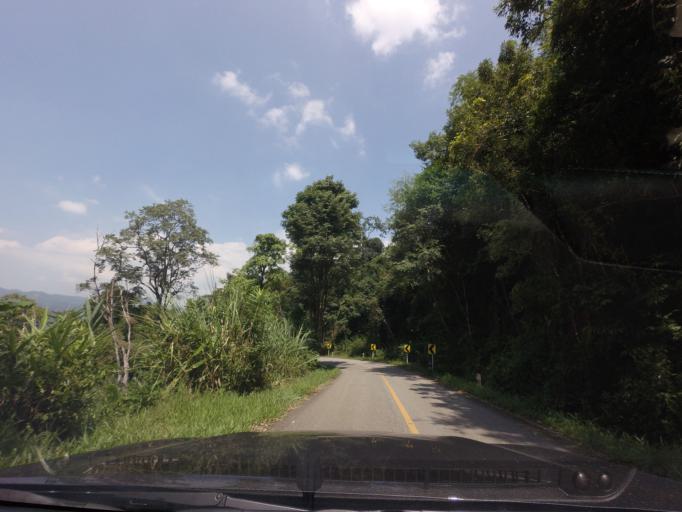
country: TH
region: Loei
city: Na Haeo
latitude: 17.6081
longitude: 100.8939
